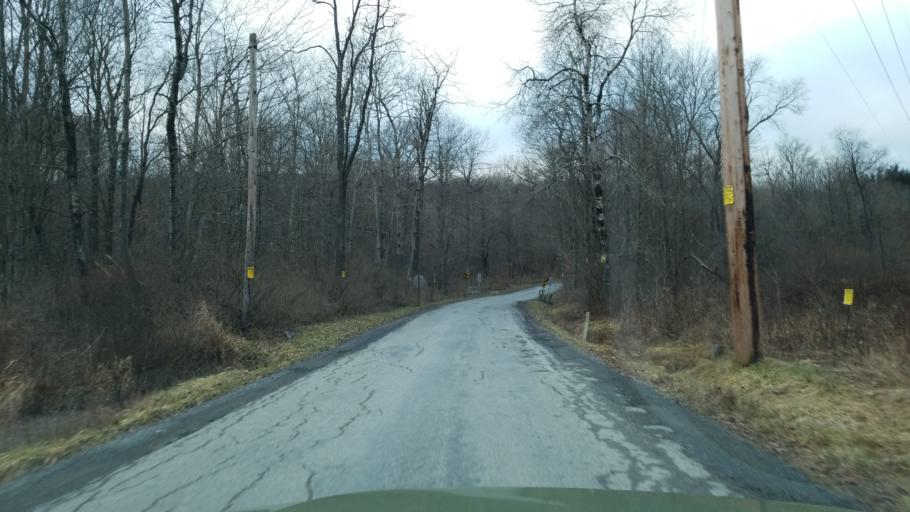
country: US
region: Pennsylvania
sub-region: Jefferson County
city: Falls Creek
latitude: 41.1731
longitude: -78.7872
